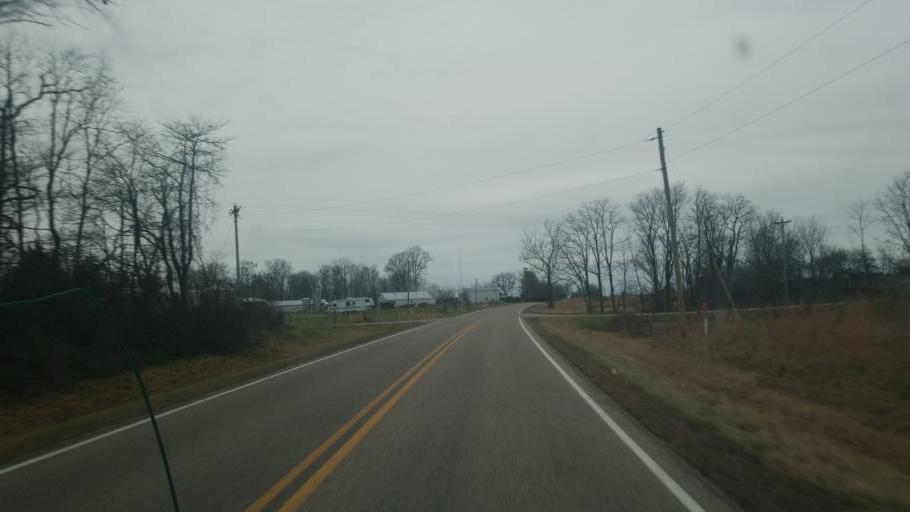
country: US
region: Indiana
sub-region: Clay County
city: Middlebury
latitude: 39.3666
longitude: -86.9694
